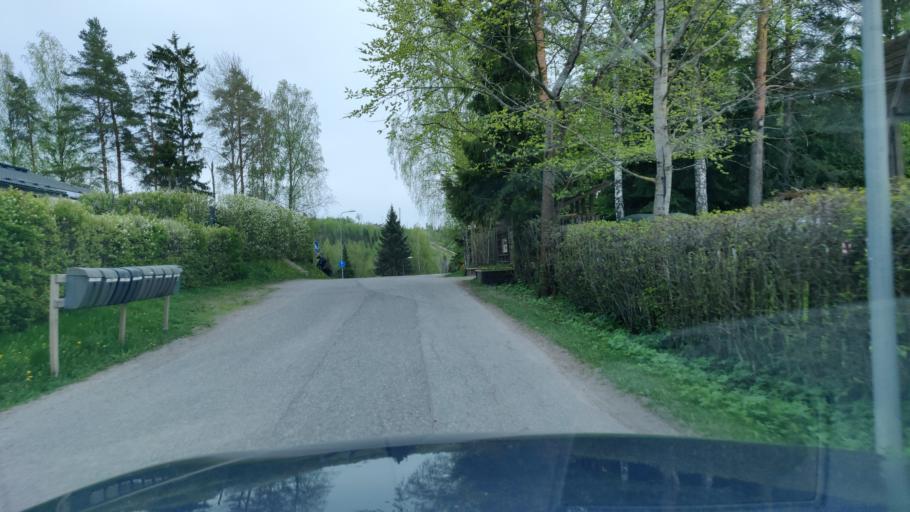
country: FI
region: Uusimaa
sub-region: Helsinki
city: Nurmijaervi
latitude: 60.3710
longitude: 24.7514
